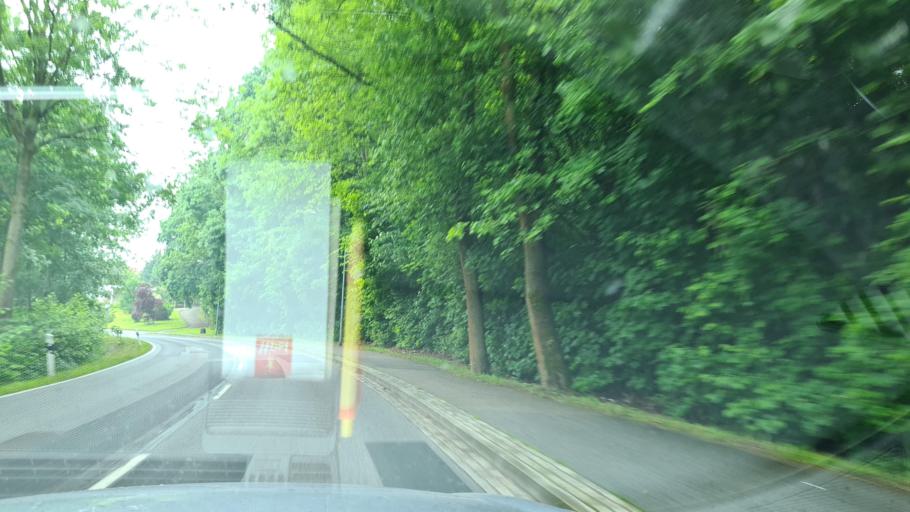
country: DE
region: Saxony
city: Schirgiswalde
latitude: 51.0834
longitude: 14.4258
